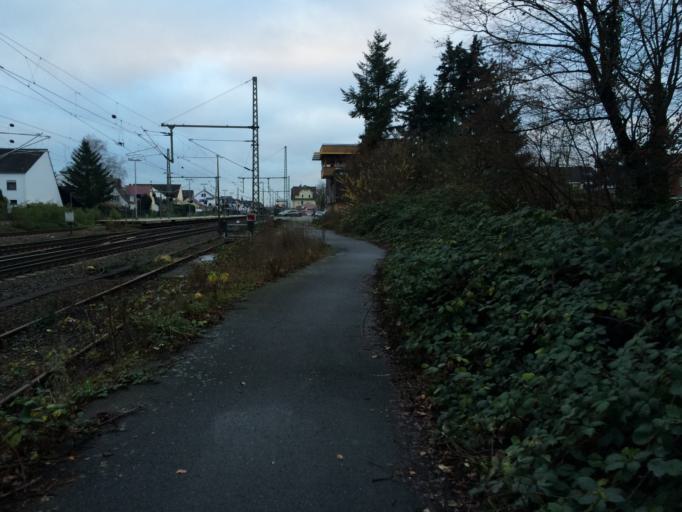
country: DE
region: Hesse
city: Morfelden-Walldorf
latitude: 50.0036
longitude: 8.5822
